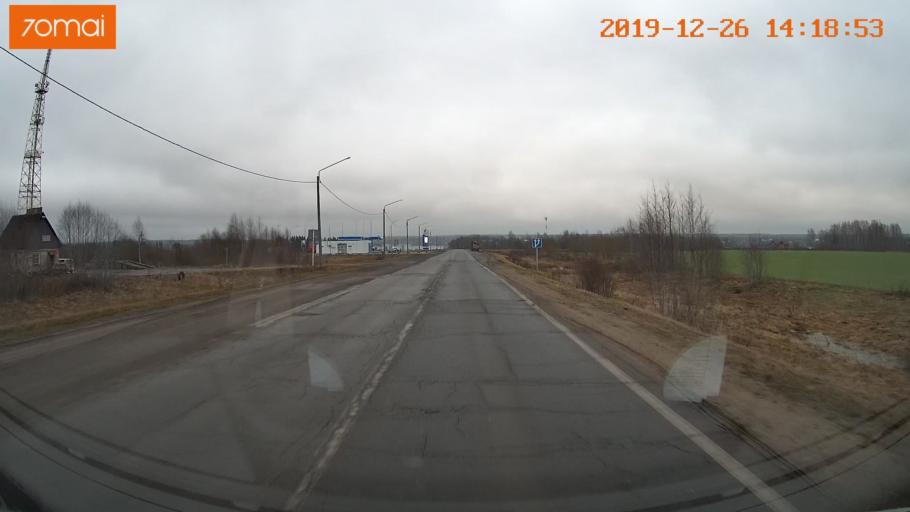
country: RU
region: Jaroslavl
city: Poshekhon'ye
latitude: 58.5130
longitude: 39.1055
